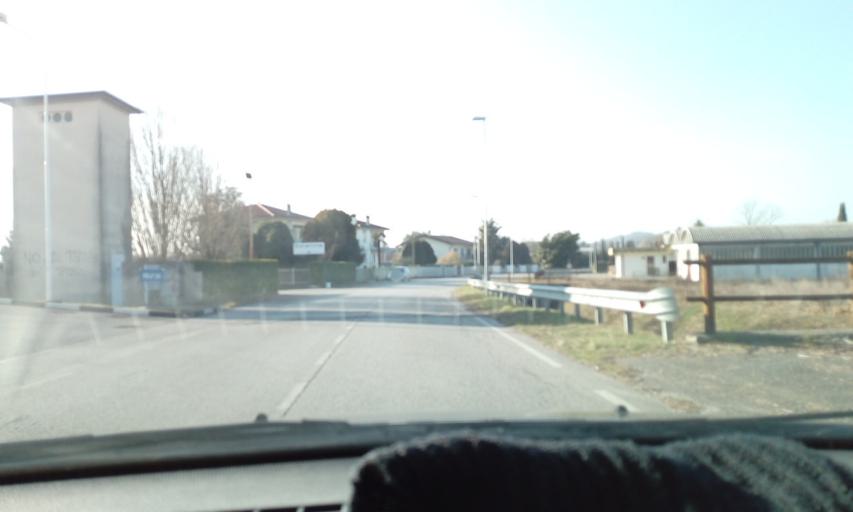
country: IT
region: Friuli Venezia Giulia
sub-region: Provincia di Udine
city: San Giovanni al Natisone
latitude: 45.9841
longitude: 13.4054
